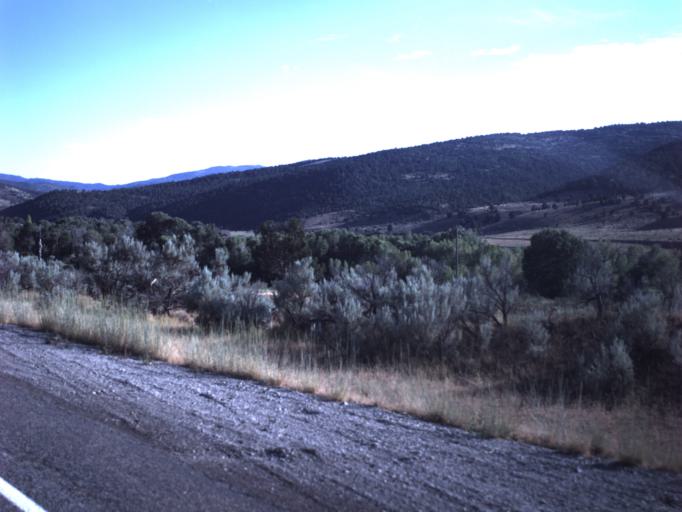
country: US
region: Utah
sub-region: Utah County
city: Woodland Hills
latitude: 39.9042
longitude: -111.5494
